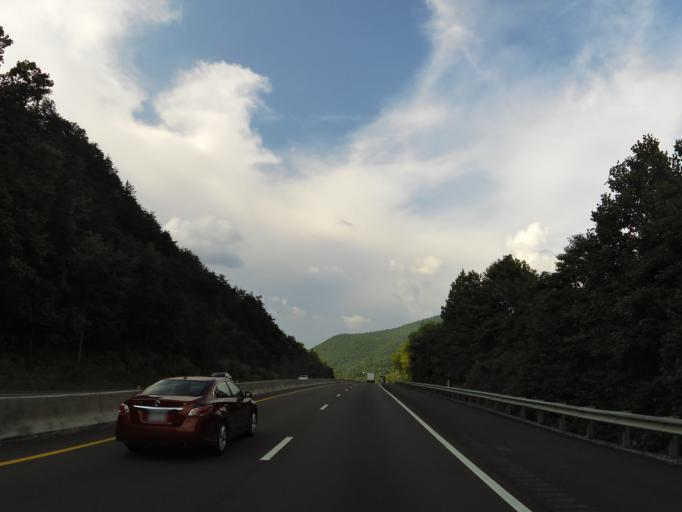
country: US
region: Tennessee
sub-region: Cocke County
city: Newport
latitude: 35.8318
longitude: -83.1827
